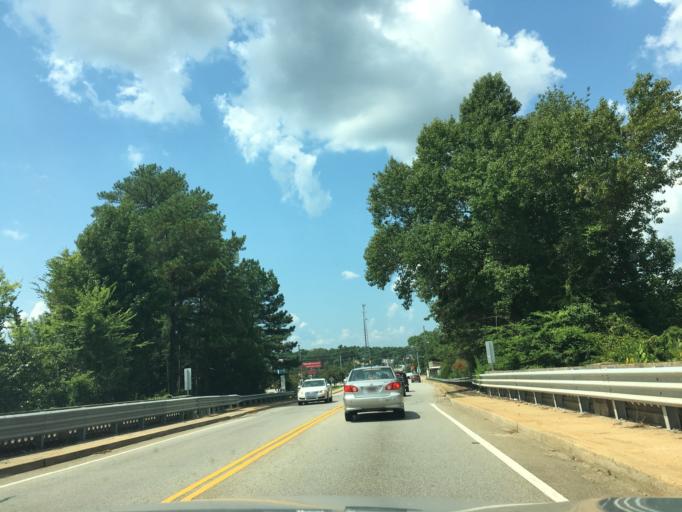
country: US
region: South Carolina
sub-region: Richland County
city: Lake Murray of Richland
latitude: 34.1255
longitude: -81.2316
